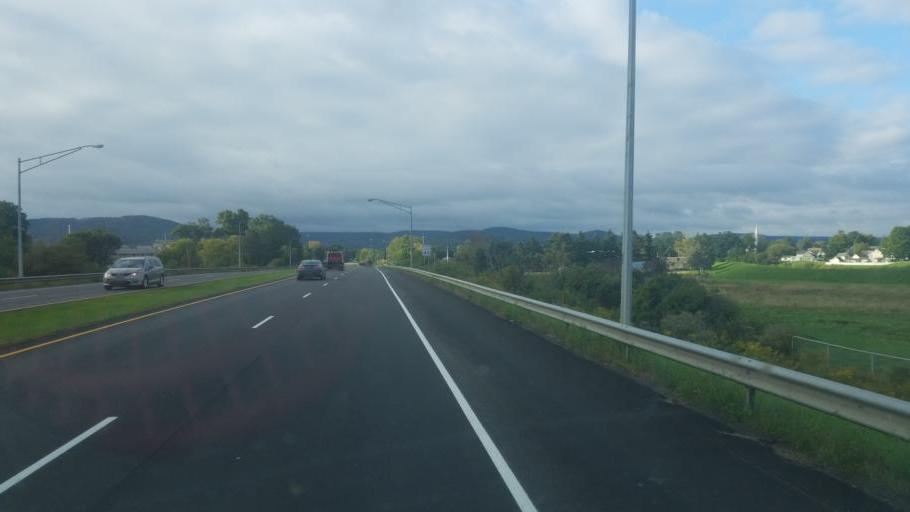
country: US
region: New York
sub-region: Cattaraugus County
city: Olean
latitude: 42.0955
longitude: -78.4276
